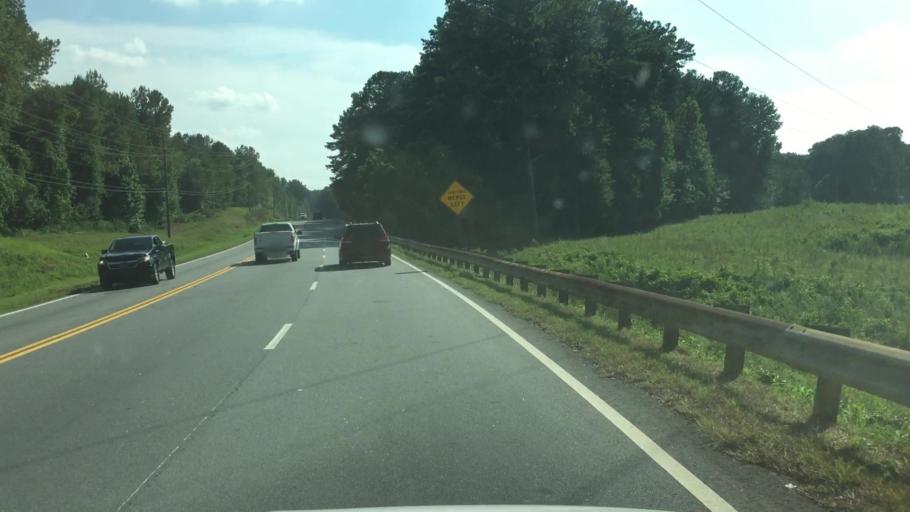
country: US
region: Georgia
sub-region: Gwinnett County
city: Dacula
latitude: 33.9985
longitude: -83.8778
